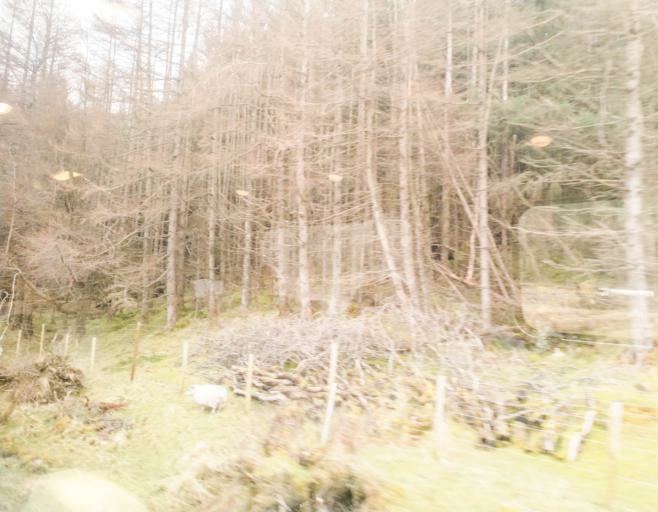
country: GB
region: Scotland
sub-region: Argyll and Bute
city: Garelochhead
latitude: 56.4454
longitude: -4.7078
